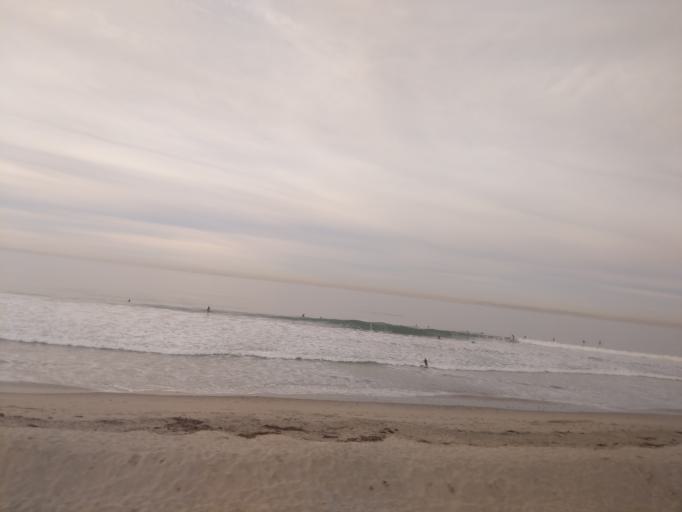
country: US
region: California
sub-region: Orange County
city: San Clemente
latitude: 33.4158
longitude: -117.6166
